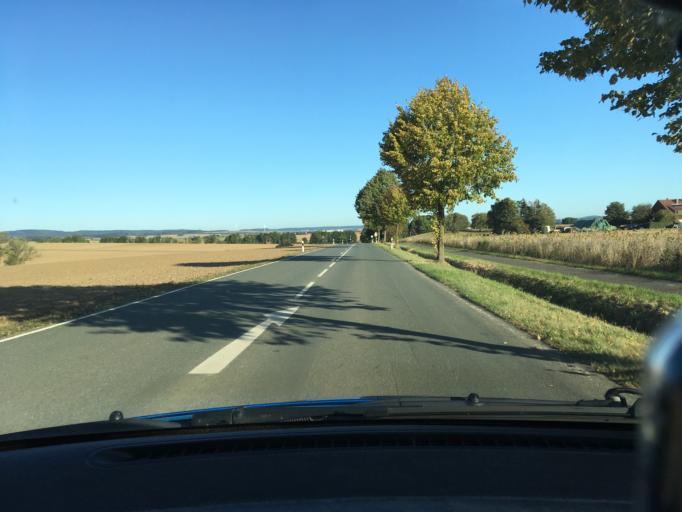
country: DE
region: Lower Saxony
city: Hulsede
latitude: 52.2272
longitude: 9.3784
